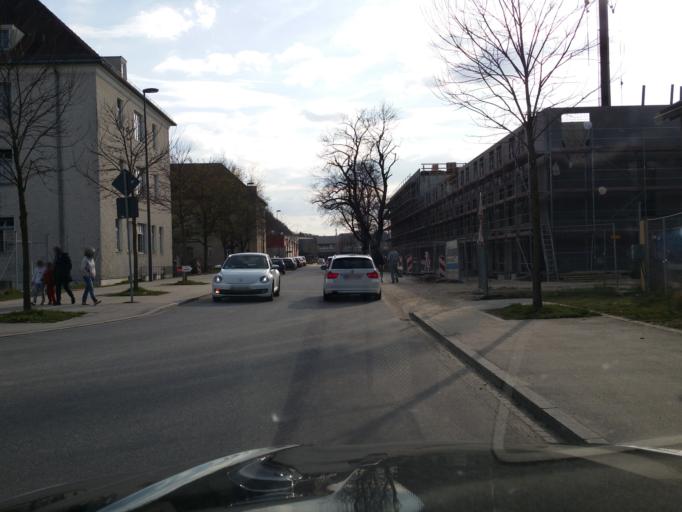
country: DE
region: Bavaria
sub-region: Lower Bavaria
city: Landshut
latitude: 48.5475
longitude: 12.1817
